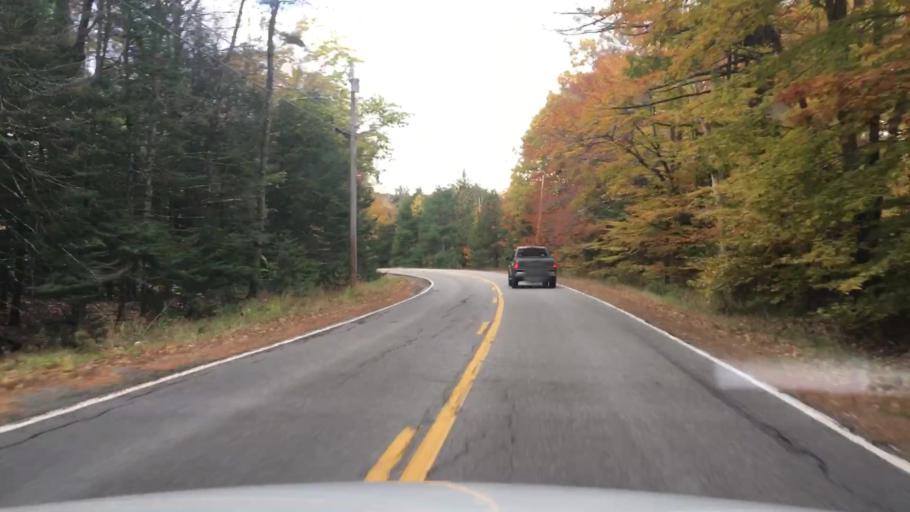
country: US
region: Maine
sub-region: Androscoggin County
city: Sabattus
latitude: 44.1359
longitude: -70.0037
